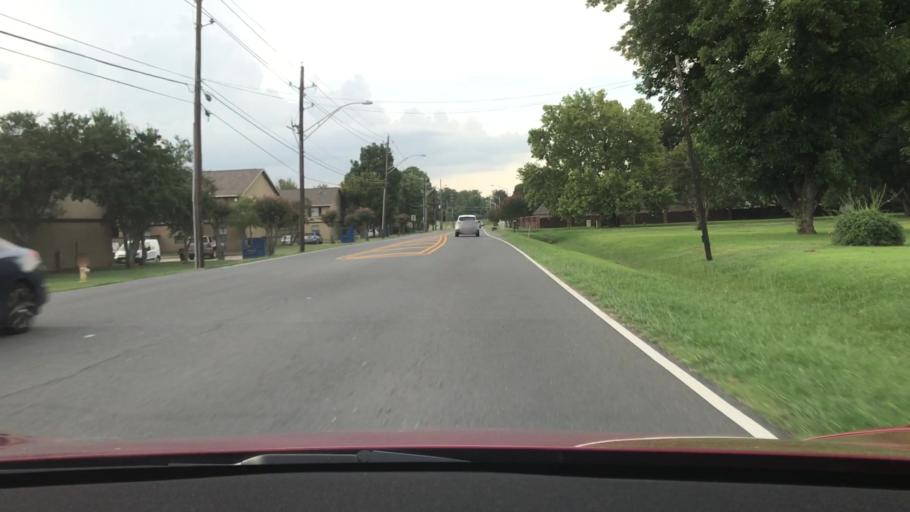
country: US
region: Louisiana
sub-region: Bossier Parish
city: Bossier City
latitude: 32.4225
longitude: -93.6942
